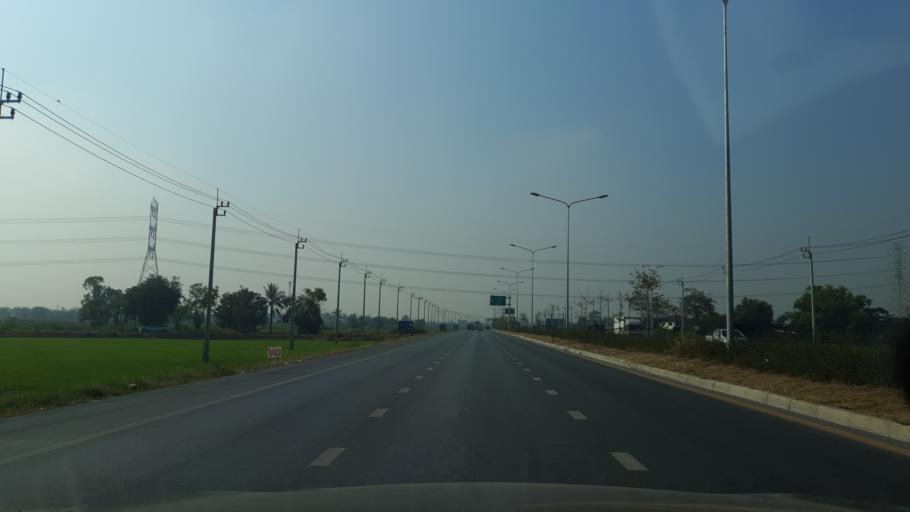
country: TH
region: Nonthaburi
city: Bang Bua Thong
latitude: 13.9725
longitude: 100.4640
